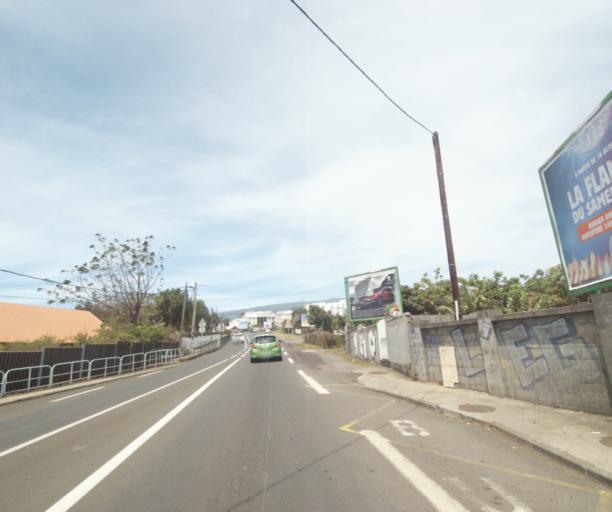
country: RE
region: Reunion
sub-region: Reunion
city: Saint-Paul
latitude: -21.0422
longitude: 55.2539
